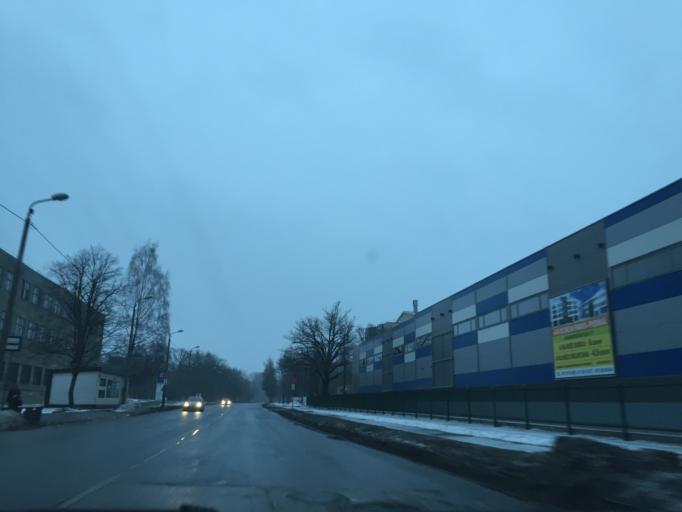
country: LV
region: Riga
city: Riga
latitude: 56.9656
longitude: 24.0715
